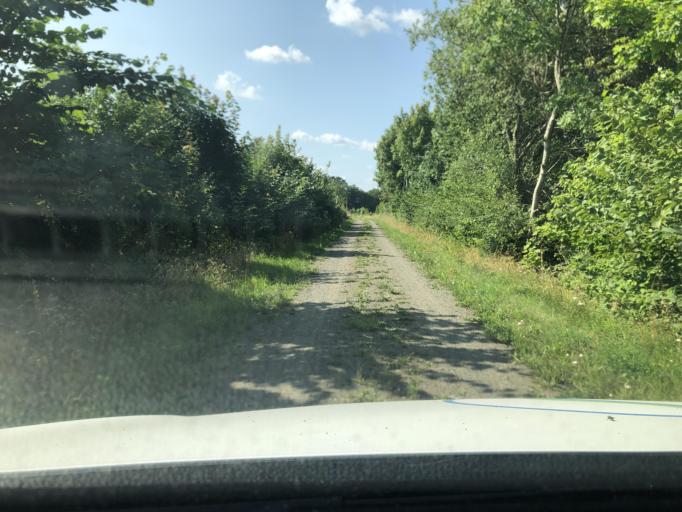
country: SE
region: Skane
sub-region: Kristianstads Kommun
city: Degeberga
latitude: 55.7992
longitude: 14.1522
